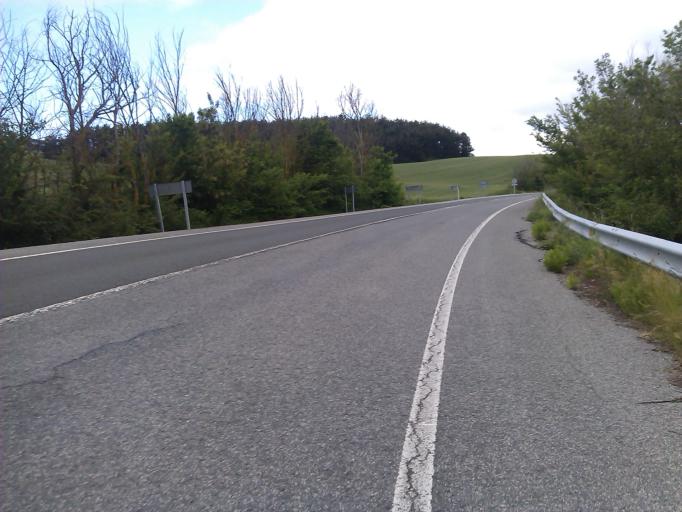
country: ES
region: Navarre
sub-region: Provincia de Navarra
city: Uterga
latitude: 42.7475
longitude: -1.7505
